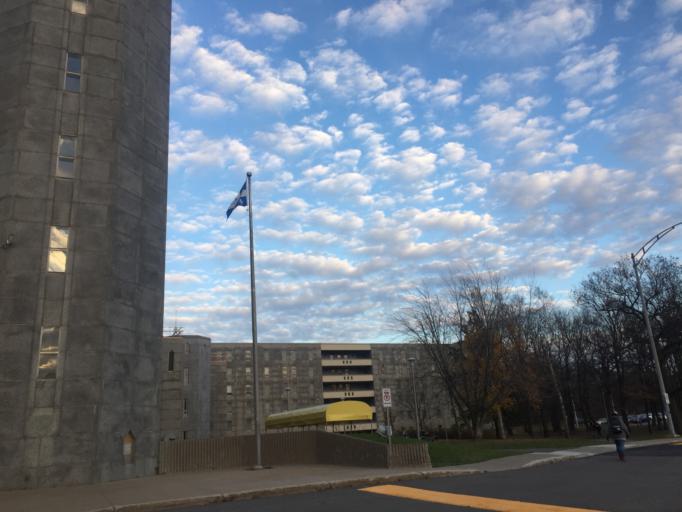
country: CA
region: Quebec
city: Quebec
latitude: 46.7821
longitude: -71.2714
